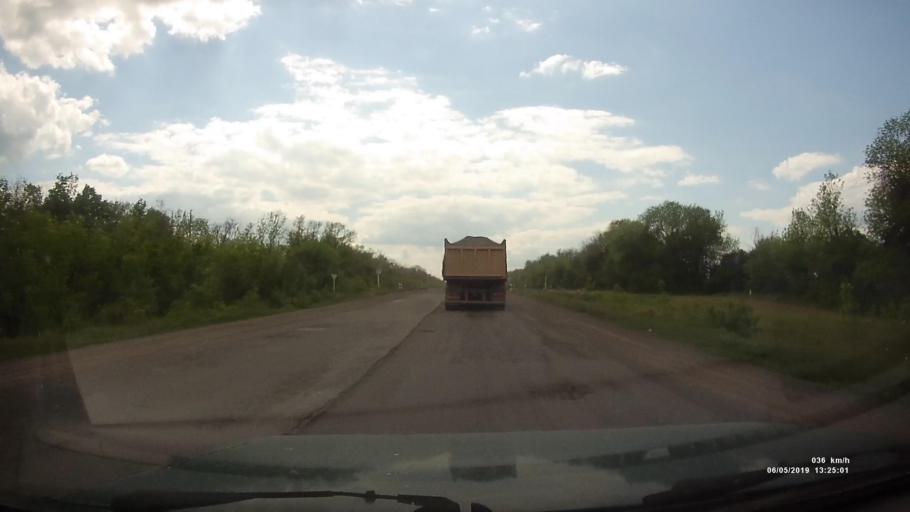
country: RU
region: Rostov
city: Ust'-Donetskiy
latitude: 47.6838
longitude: 40.9066
